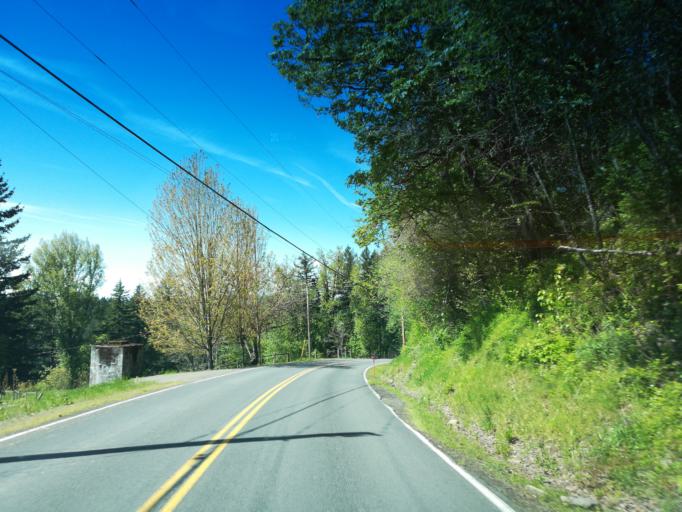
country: US
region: Oregon
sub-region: Multnomah County
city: Troutdale
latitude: 45.5256
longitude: -122.3679
